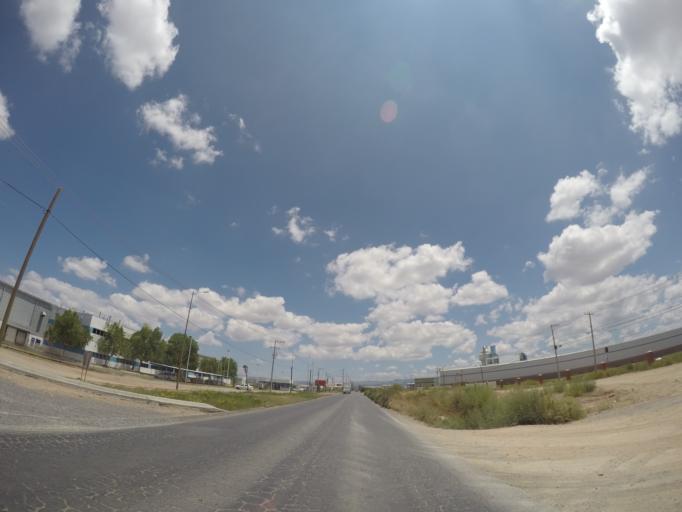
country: MX
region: San Luis Potosi
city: La Pila
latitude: 22.0437
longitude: -100.8815
